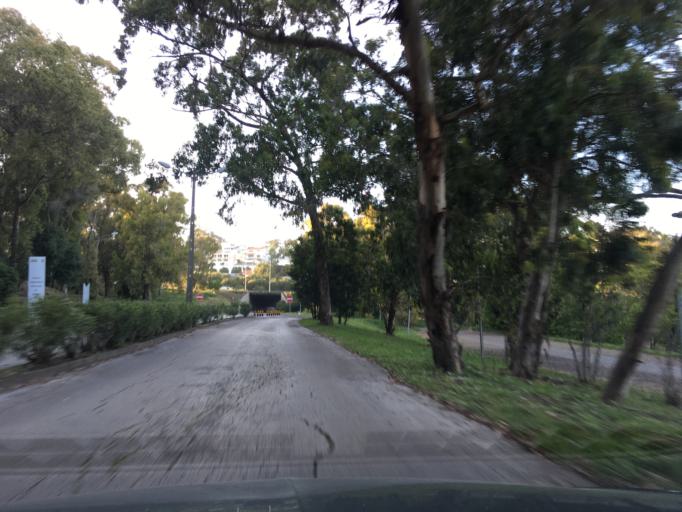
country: PT
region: Lisbon
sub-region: Oeiras
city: Quejas
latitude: 38.7116
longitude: -9.2593
